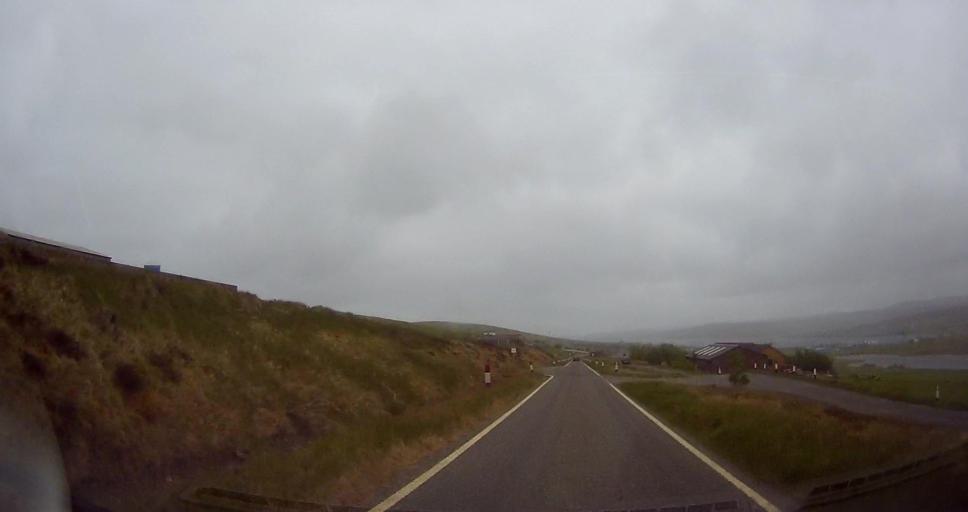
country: GB
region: Scotland
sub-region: Shetland Islands
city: Lerwick
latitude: 60.2757
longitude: -1.3903
